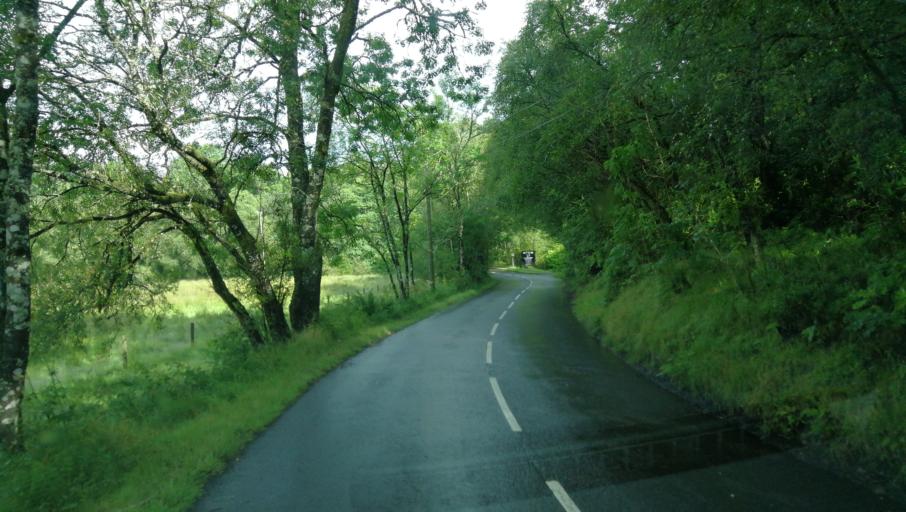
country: GB
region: Scotland
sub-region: Stirling
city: Callander
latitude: 56.2290
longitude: -4.3705
